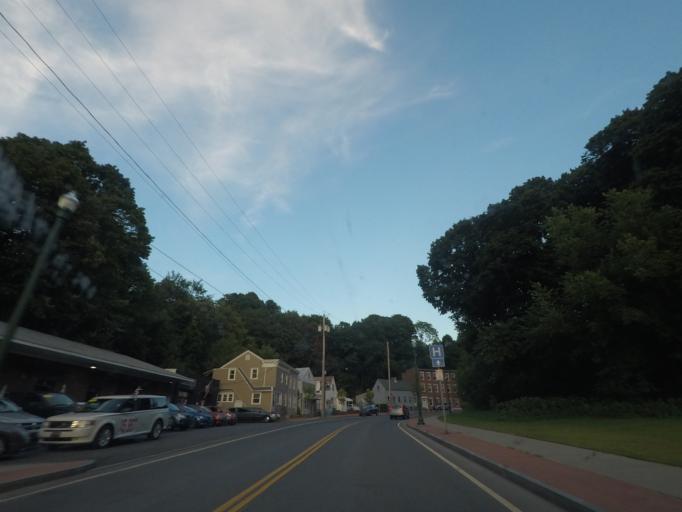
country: US
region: New York
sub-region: Rensselaer County
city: Troy
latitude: 42.7269
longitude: -73.6825
